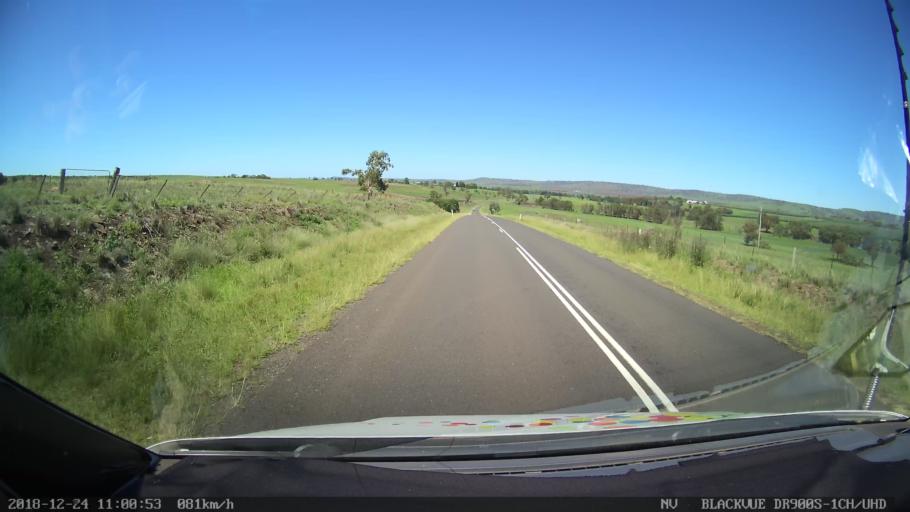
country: AU
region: New South Wales
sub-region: Upper Hunter Shire
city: Merriwa
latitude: -32.0716
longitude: 150.3898
